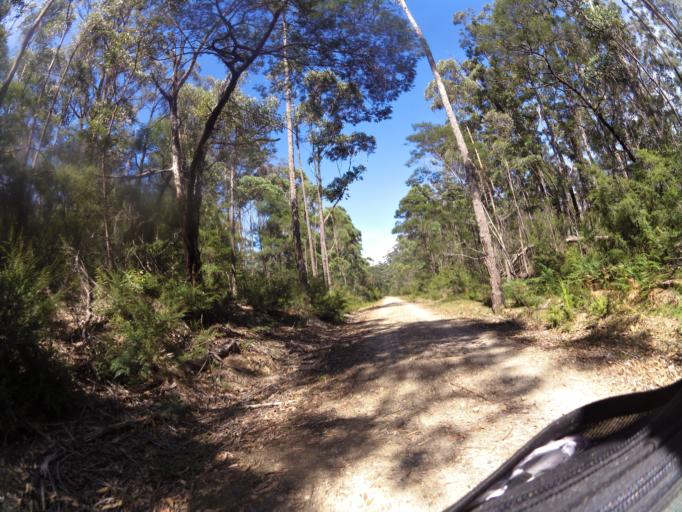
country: AU
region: Victoria
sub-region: East Gippsland
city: Lakes Entrance
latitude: -37.7222
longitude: 148.1146
